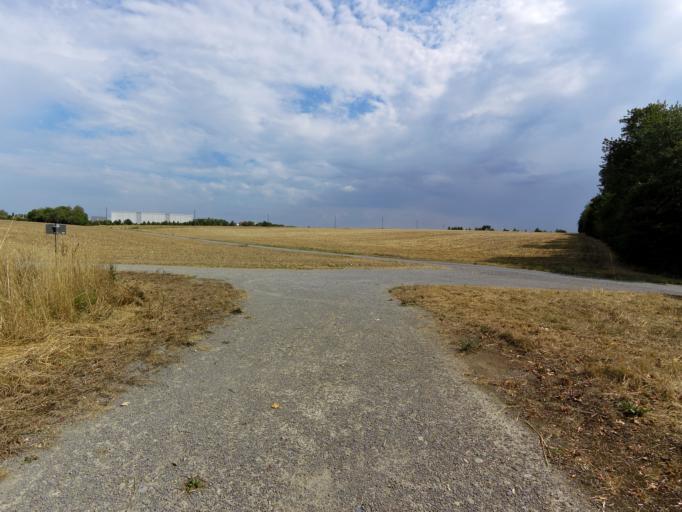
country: DE
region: Bavaria
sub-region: Regierungsbezirk Unterfranken
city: Waldbuttelbrunn
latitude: 49.7939
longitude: 9.8348
